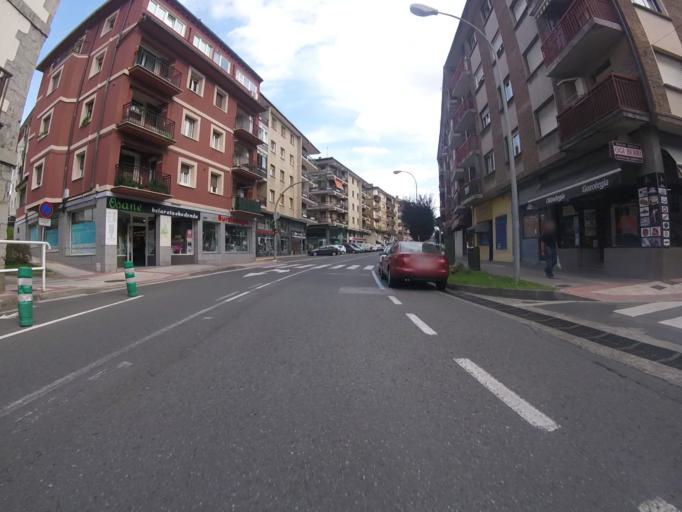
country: ES
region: Basque Country
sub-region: Provincia de Guipuzcoa
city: Urnieta
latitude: 43.2484
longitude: -1.9926
